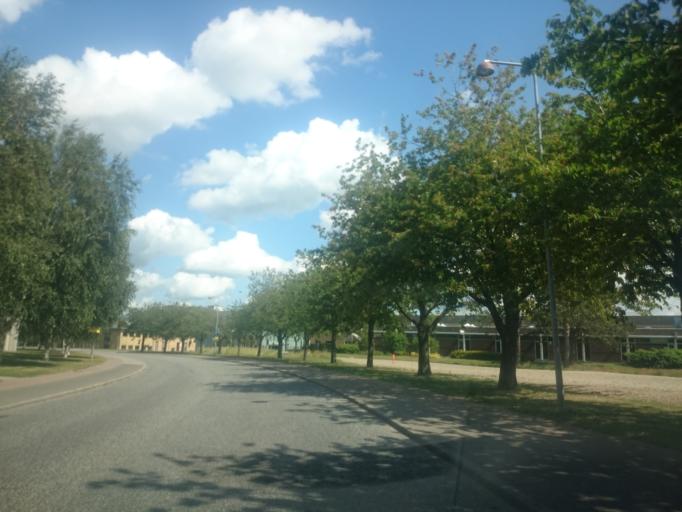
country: DK
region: South Denmark
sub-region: Billund Kommune
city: Billund
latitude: 55.7321
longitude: 9.1186
